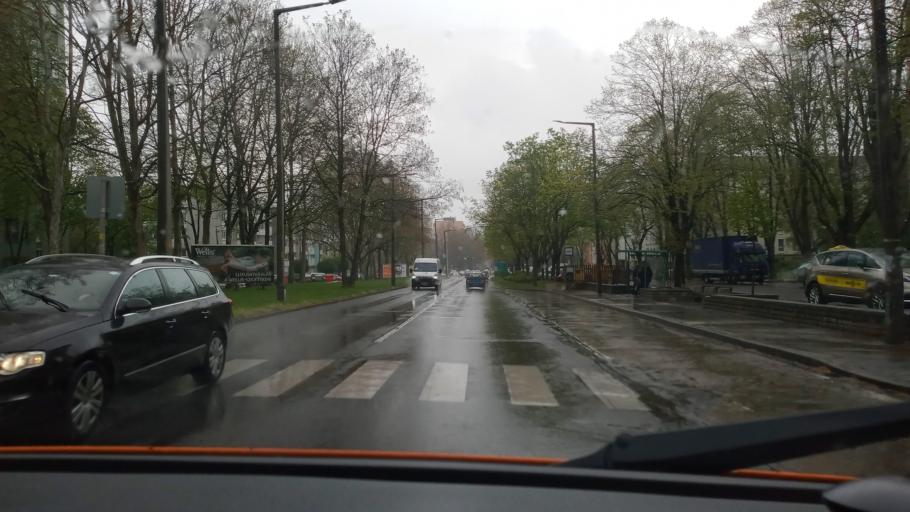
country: HU
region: Baranya
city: Pecs
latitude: 46.0402
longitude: 18.2172
